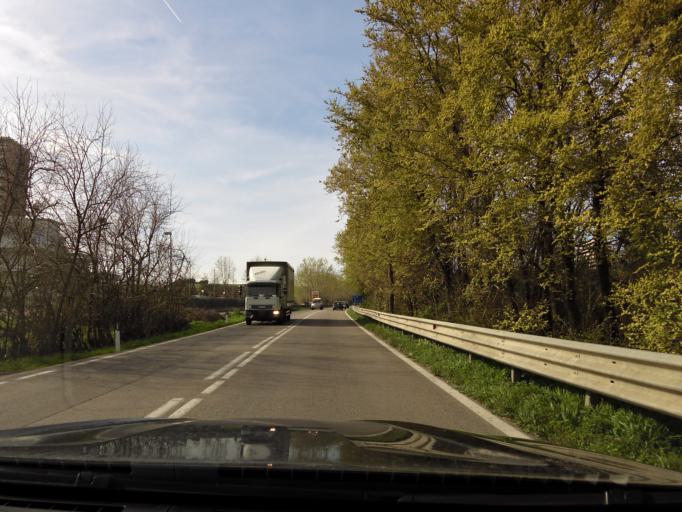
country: IT
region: The Marches
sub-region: Provincia di Macerata
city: Porto Recanati
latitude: 43.4168
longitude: 13.6683
